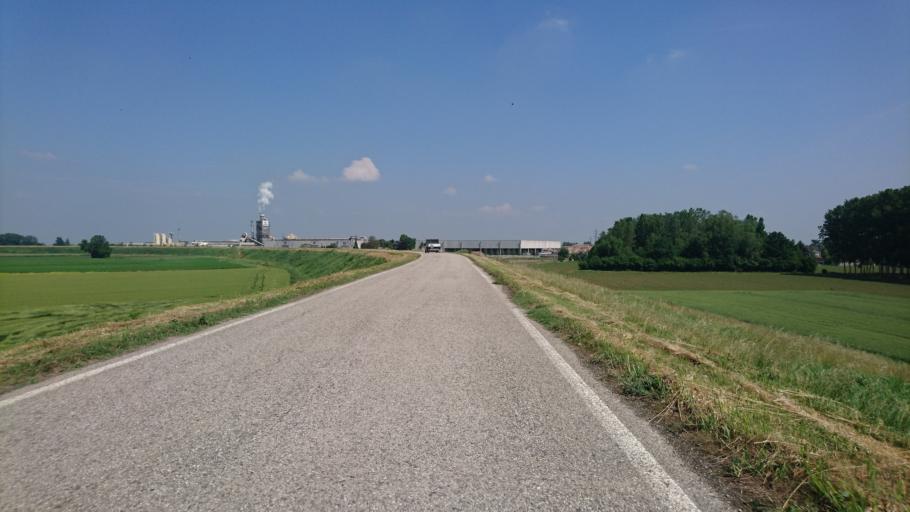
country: IT
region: Lombardy
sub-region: Provincia di Mantova
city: Quingentole
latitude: 45.0632
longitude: 11.0493
